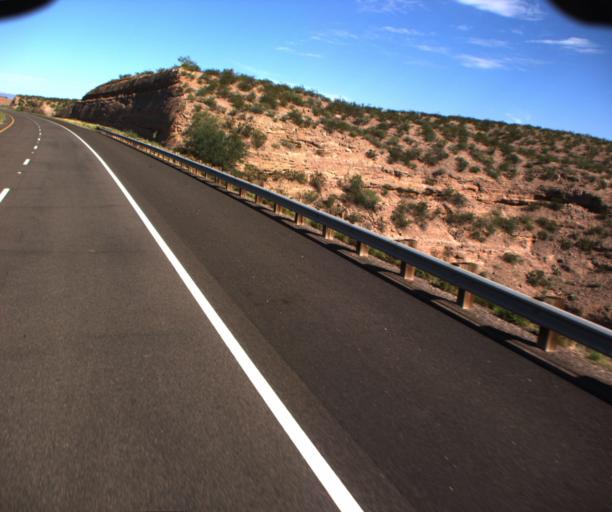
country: US
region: Arizona
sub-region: Greenlee County
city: Clifton
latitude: 32.9724
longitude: -109.2406
